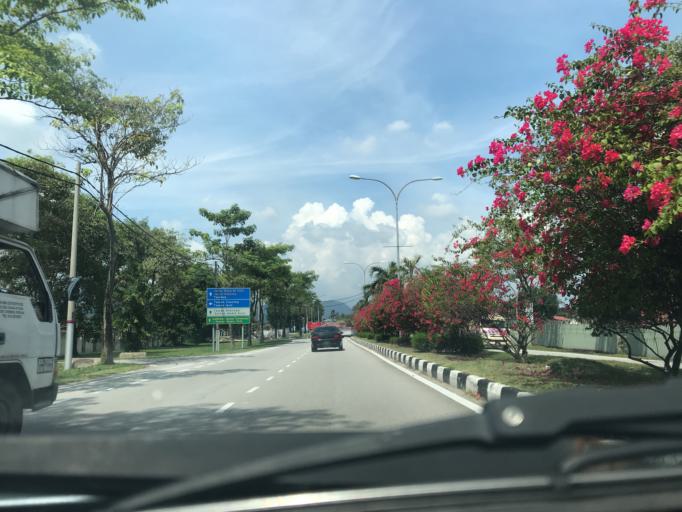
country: MY
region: Perak
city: Ipoh
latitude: 4.6020
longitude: 101.1026
